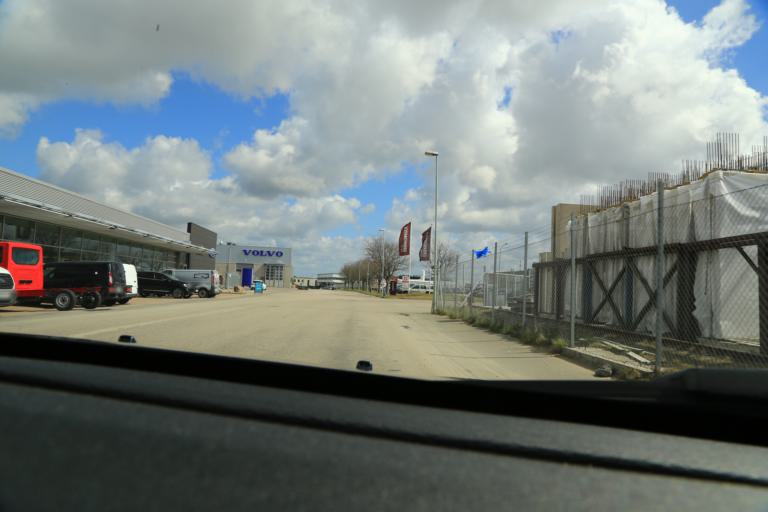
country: SE
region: Halland
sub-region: Varbergs Kommun
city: Varberg
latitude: 57.1221
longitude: 12.2820
